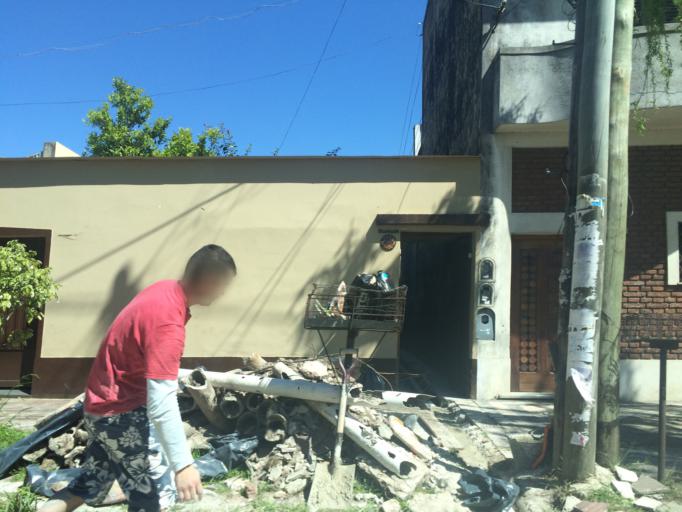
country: AR
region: Buenos Aires
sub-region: Partido de Lanus
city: Lanus
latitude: -34.7157
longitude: -58.3979
